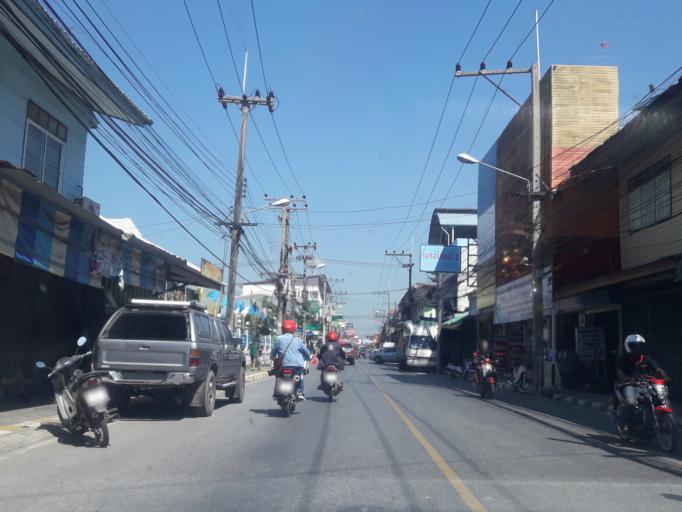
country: TH
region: Sara Buri
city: Nong Khae
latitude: 14.3385
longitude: 100.8668
